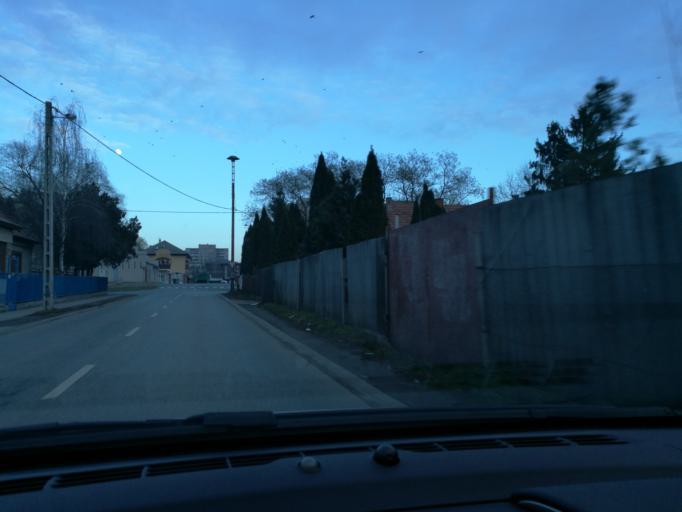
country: HU
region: Szabolcs-Szatmar-Bereg
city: Nyiregyhaza
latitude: 47.9590
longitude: 21.7347
